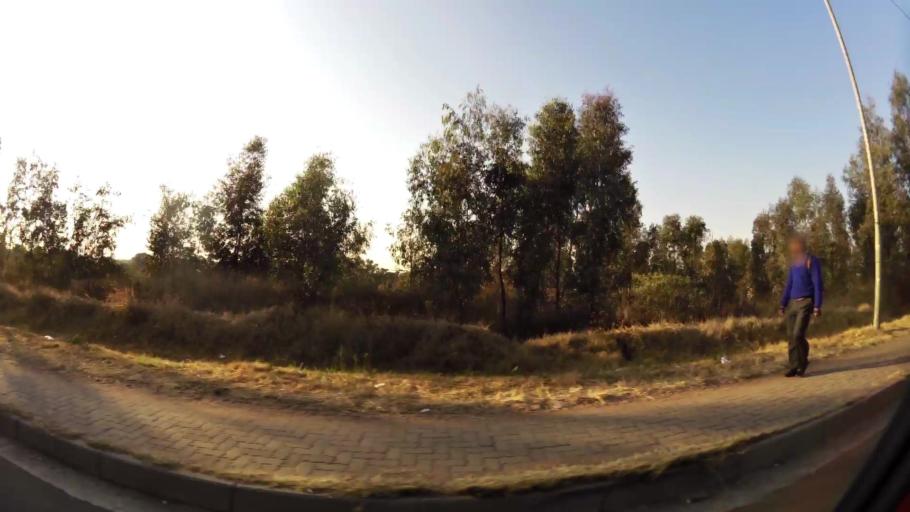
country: ZA
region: Gauteng
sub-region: City of Johannesburg Metropolitan Municipality
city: Johannesburg
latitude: -26.2132
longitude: 27.9881
